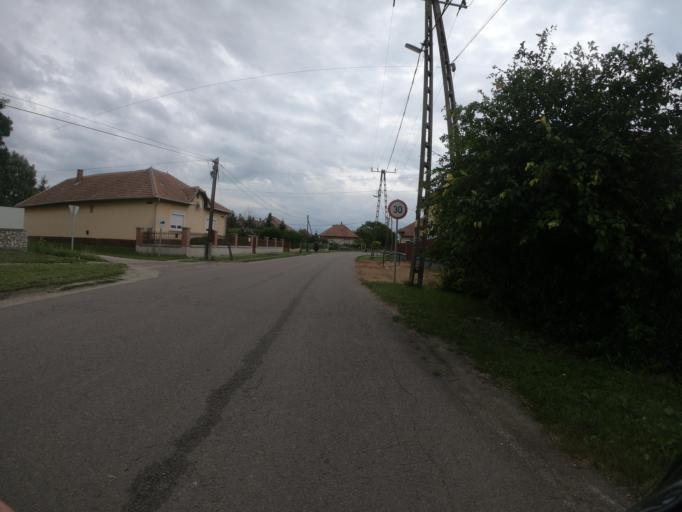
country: HU
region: Borsod-Abauj-Zemplen
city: Szentistvan
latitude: 47.7728
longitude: 20.6616
